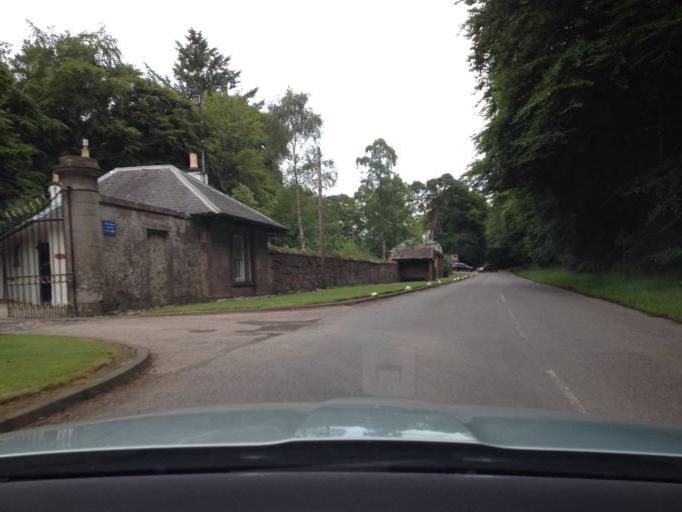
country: GB
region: Scotland
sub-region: Angus
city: Brechin
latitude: 56.8283
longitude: -2.6559
